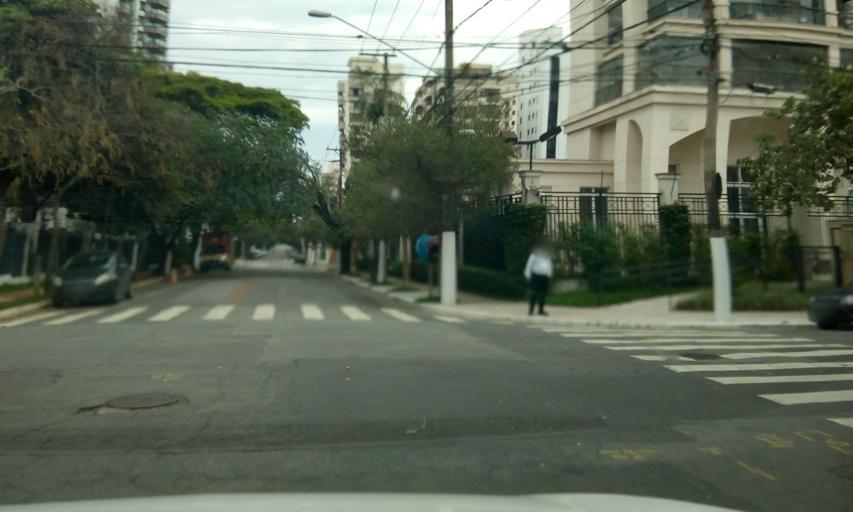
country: BR
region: Sao Paulo
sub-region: Sao Paulo
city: Sao Paulo
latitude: -23.6096
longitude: -46.6574
